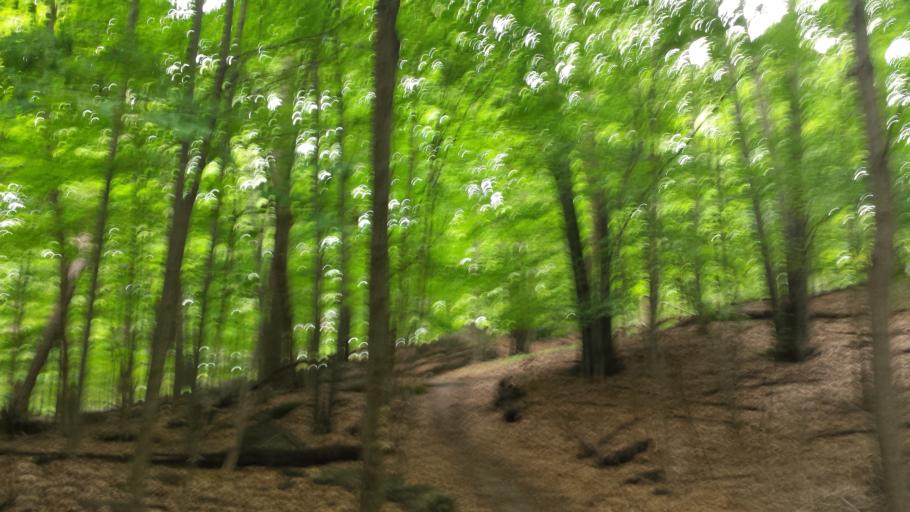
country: US
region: New York
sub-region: Westchester County
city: Buchanan
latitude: 41.2675
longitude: -73.9215
